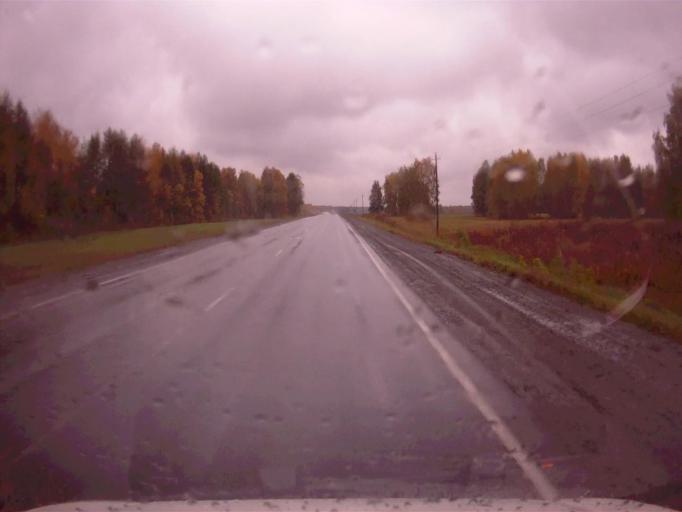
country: RU
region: Chelyabinsk
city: Roshchino
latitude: 55.4013
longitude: 61.0712
